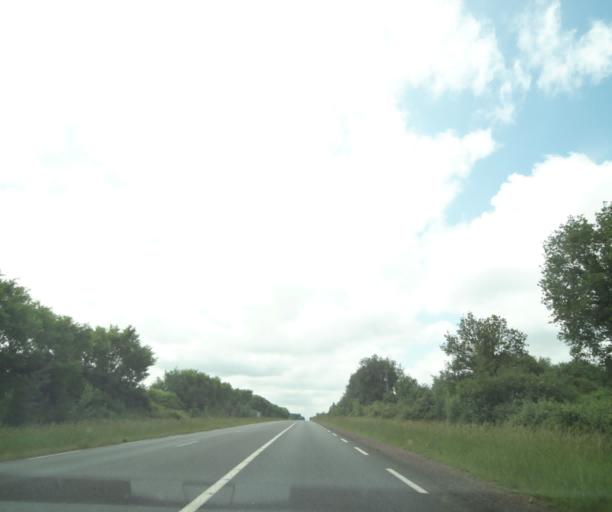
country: FR
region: Poitou-Charentes
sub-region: Departement des Deux-Sevres
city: Airvault
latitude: 46.8063
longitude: -0.2118
